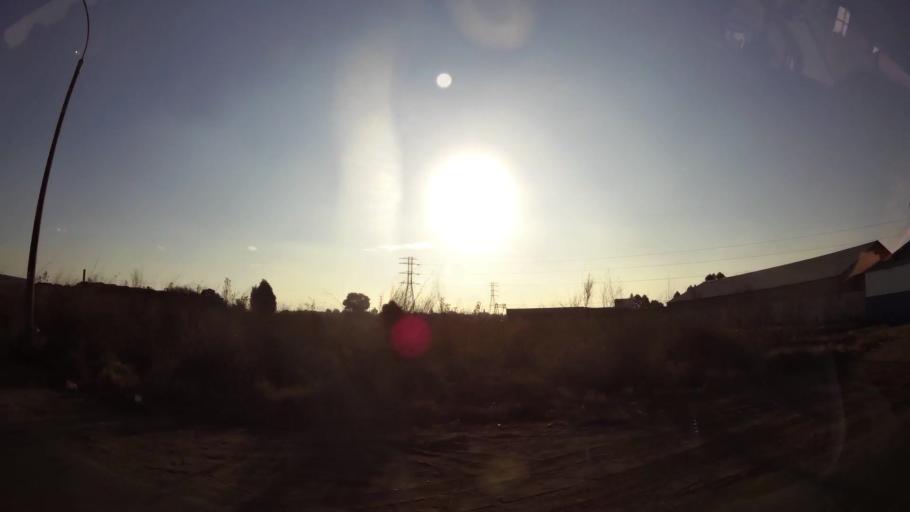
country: ZA
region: Gauteng
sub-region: West Rand District Municipality
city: Randfontein
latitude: -26.1934
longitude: 27.6863
